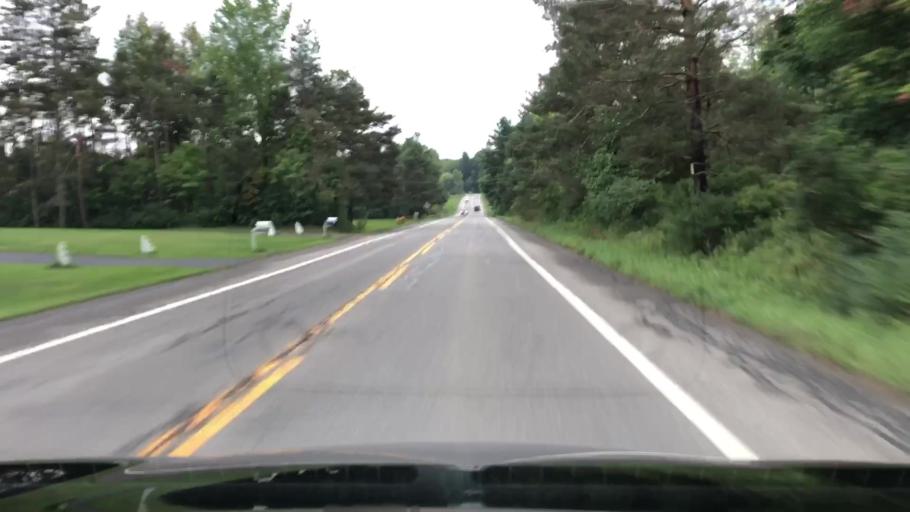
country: US
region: New York
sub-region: Erie County
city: Orchard Park
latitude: 42.7579
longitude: -78.6969
